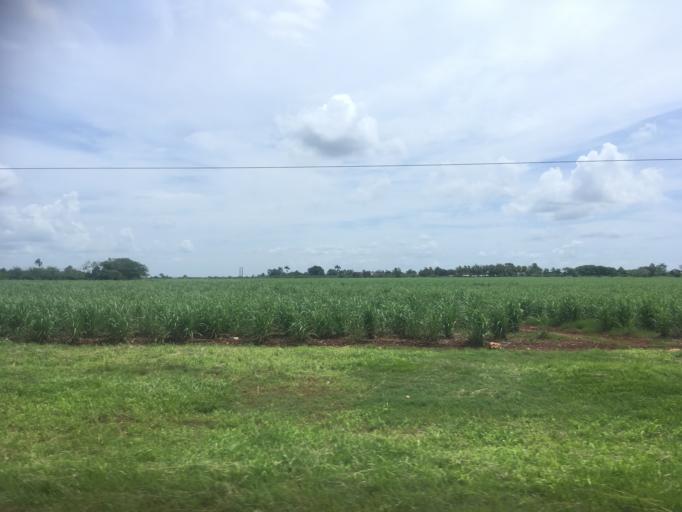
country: CU
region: Matanzas
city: Perico
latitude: 22.7802
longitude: -81.0387
